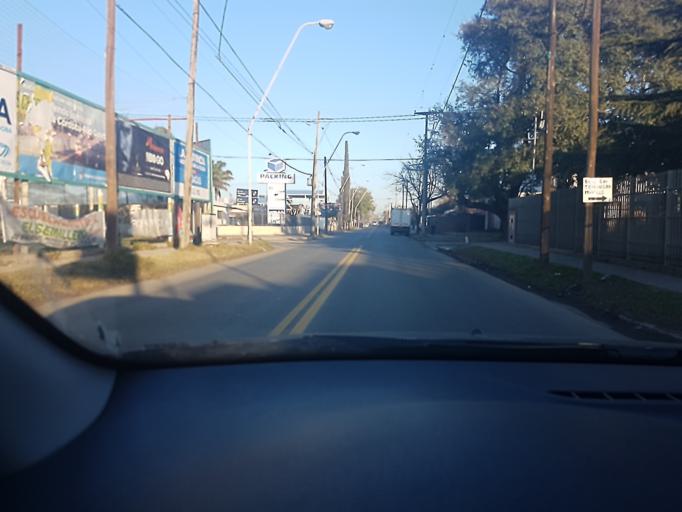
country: AR
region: Cordoba
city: Villa Allende
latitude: -31.3433
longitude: -64.2289
